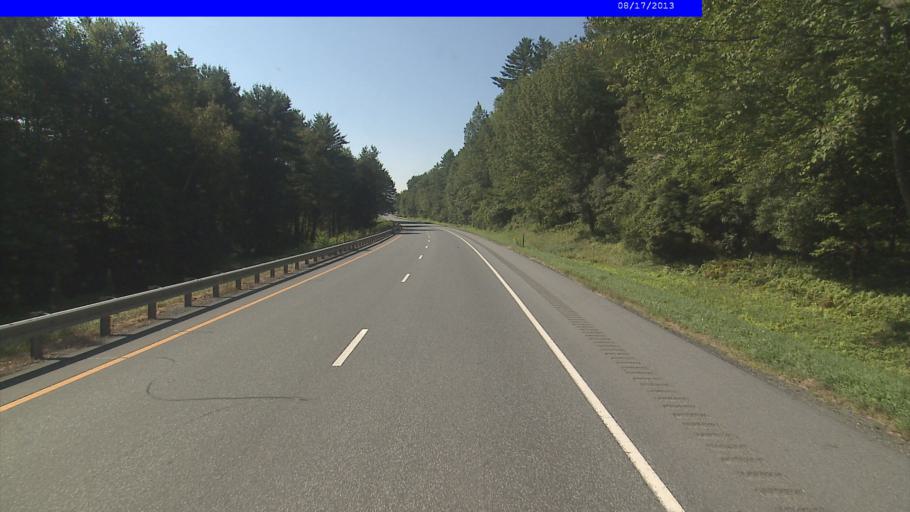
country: US
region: Vermont
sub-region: Windsor County
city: Windsor
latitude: 43.5714
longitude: -72.3866
